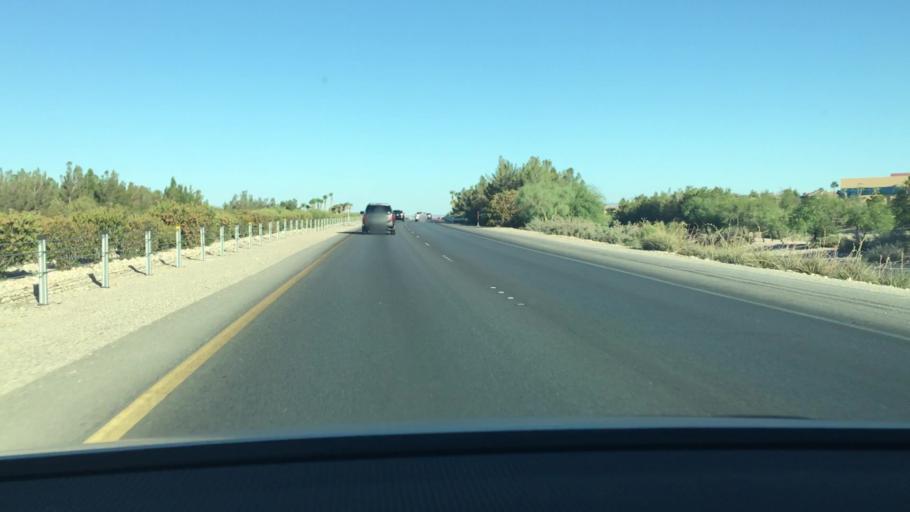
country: US
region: Nevada
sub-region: Clark County
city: Summerlin South
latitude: 36.1890
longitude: -115.3097
